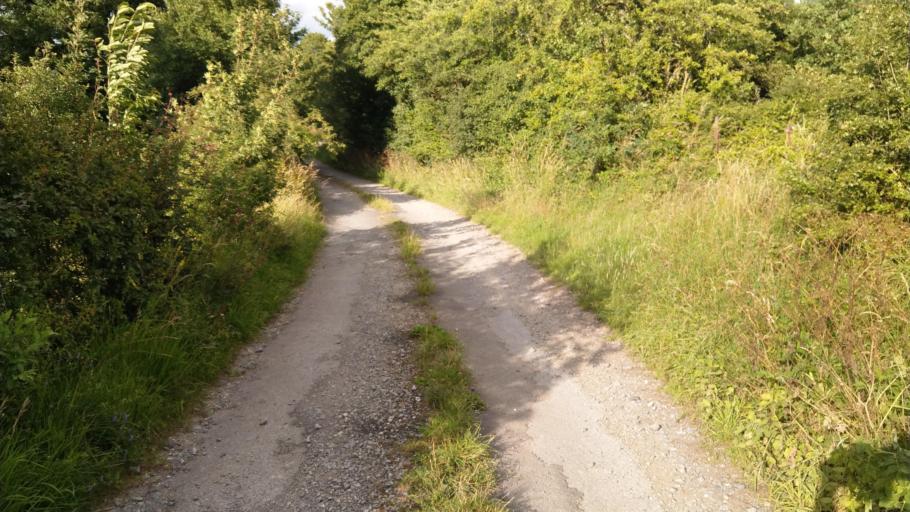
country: BE
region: Wallonia
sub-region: Province de Namur
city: Couvin
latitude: 50.0685
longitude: 4.4482
